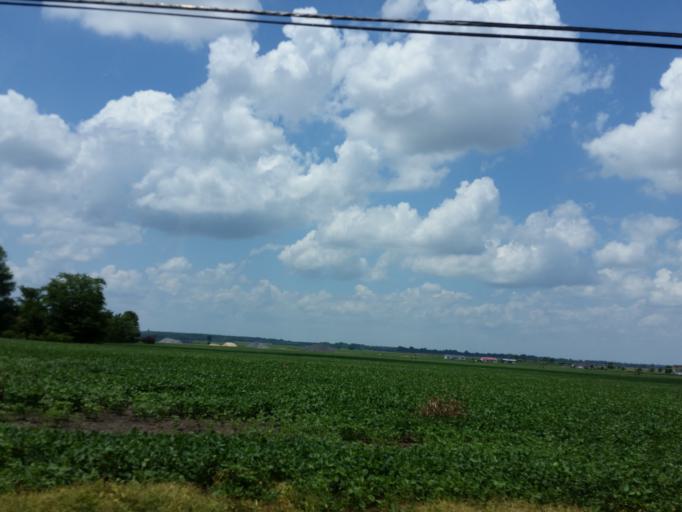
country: US
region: Tennessee
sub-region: Lake County
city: Ridgely
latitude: 36.2731
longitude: -89.4779
